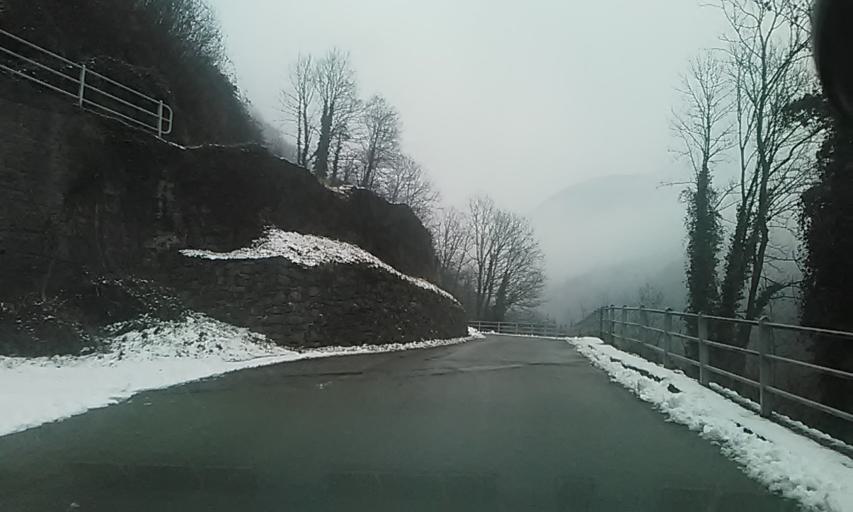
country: IT
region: Piedmont
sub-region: Provincia di Vercelli
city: Varallo
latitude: 45.8377
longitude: 8.2619
